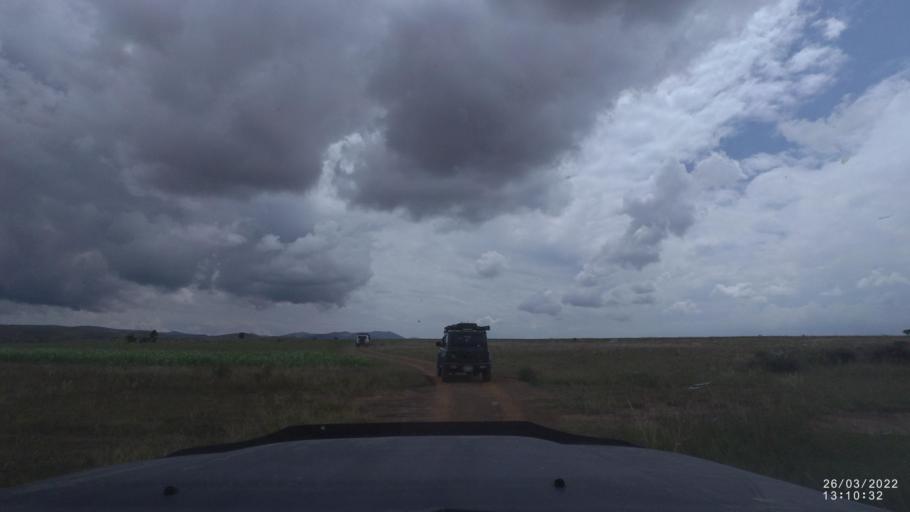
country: BO
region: Cochabamba
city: Cliza
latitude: -17.7373
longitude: -65.8570
